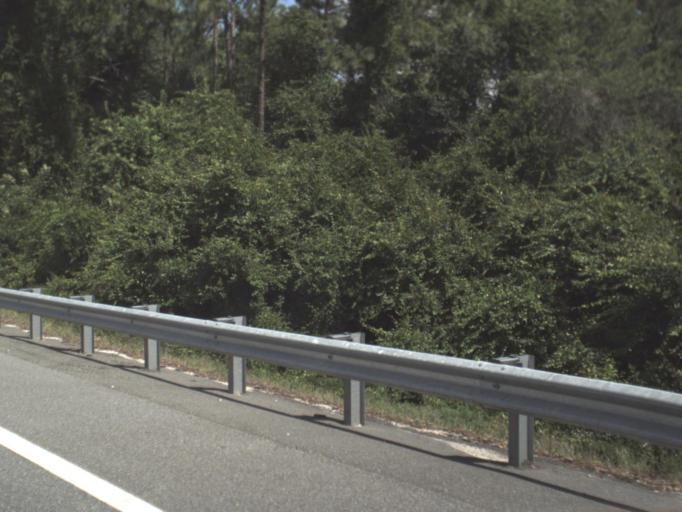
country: US
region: Florida
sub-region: Putnam County
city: Interlachen
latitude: 29.7234
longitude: -81.8315
